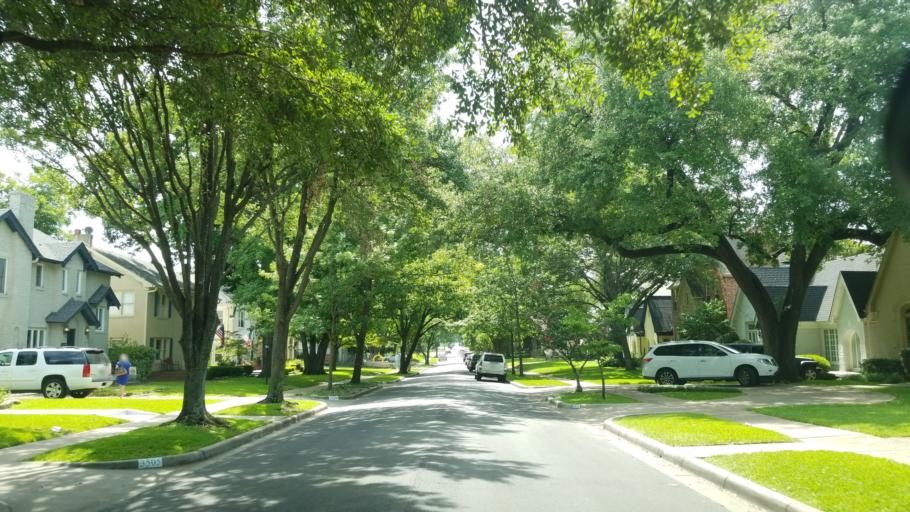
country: US
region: Texas
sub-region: Dallas County
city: University Park
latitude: 32.8530
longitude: -96.7904
